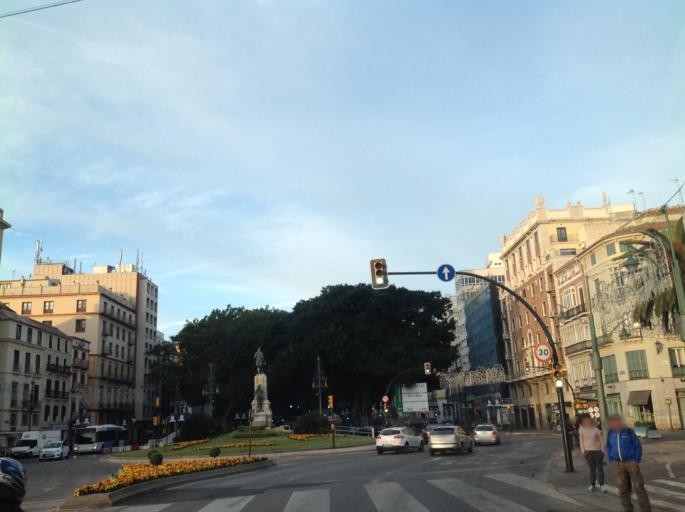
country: ES
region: Andalusia
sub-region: Provincia de Malaga
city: Malaga
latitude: 36.7182
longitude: -4.4208
